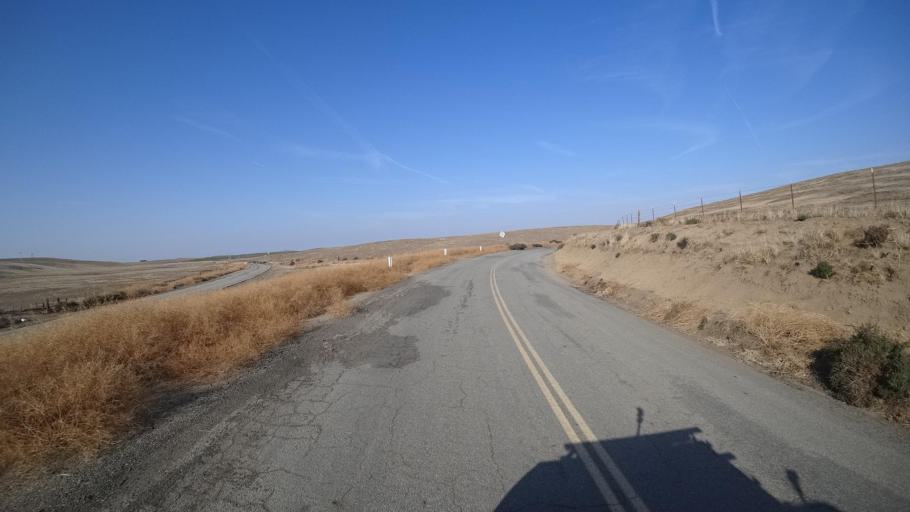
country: US
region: California
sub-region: Tulare County
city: Richgrove
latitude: 35.6215
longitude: -119.0289
